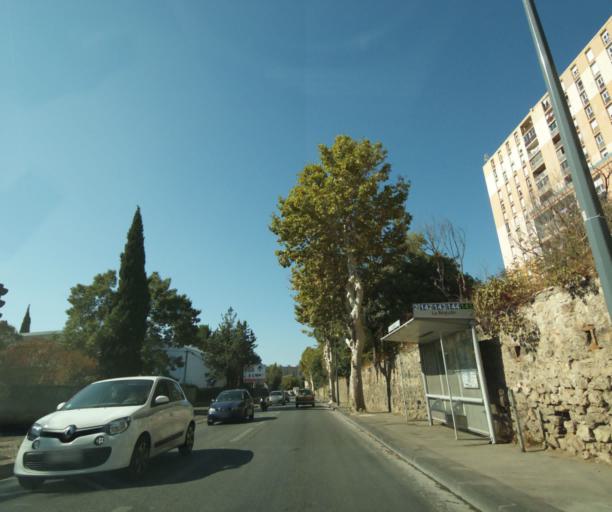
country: FR
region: Provence-Alpes-Cote d'Azur
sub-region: Departement des Bouches-du-Rhone
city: Plan-de-Cuques
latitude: 43.3332
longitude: 5.4380
